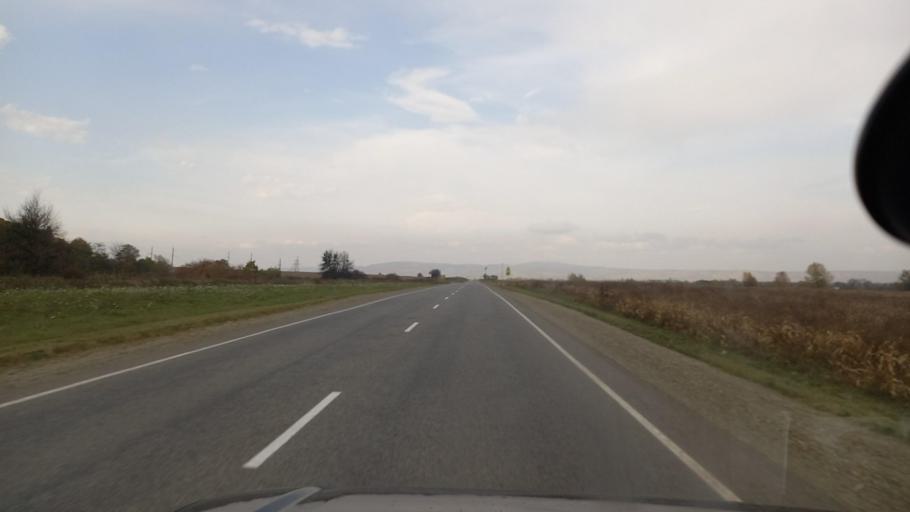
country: RU
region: Krasnodarskiy
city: Shedok
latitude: 44.2461
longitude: 40.8626
